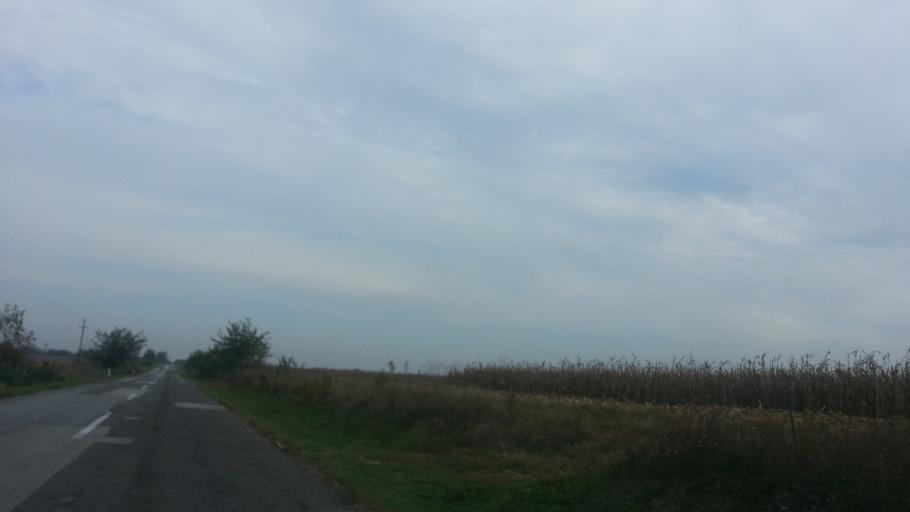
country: RS
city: Surduk
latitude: 45.0547
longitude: 20.3314
